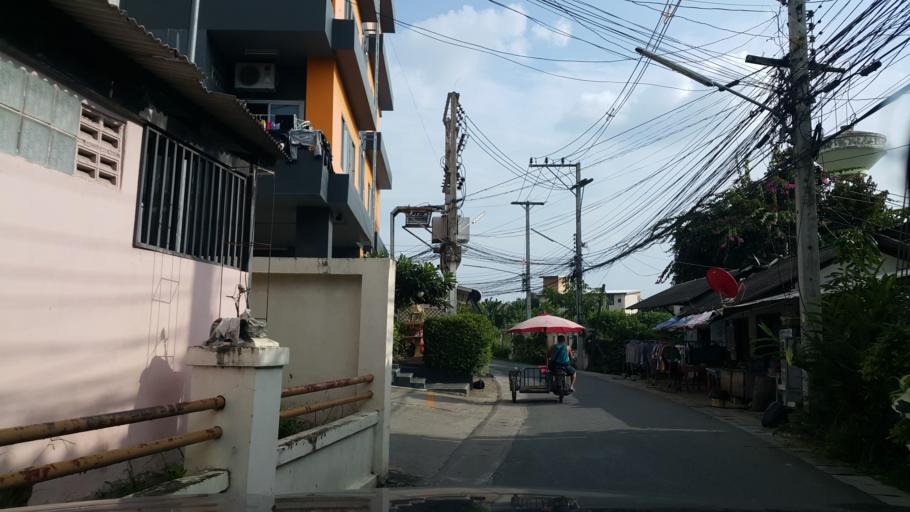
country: TH
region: Chiang Mai
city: Chiang Mai
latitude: 18.7929
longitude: 99.0251
